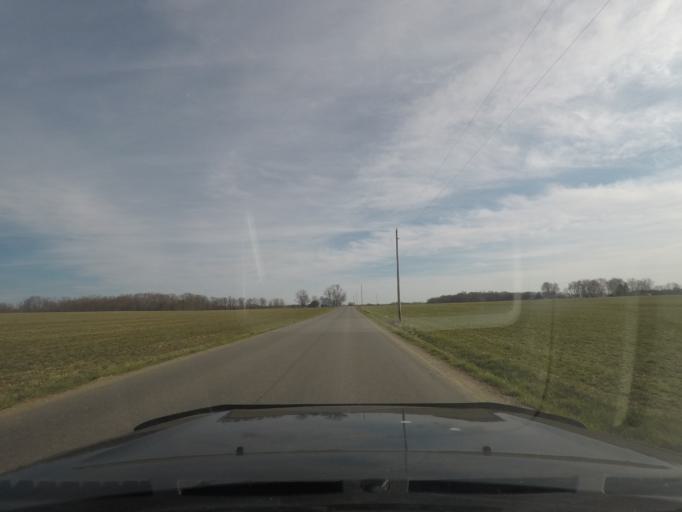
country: US
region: Indiana
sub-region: Elkhart County
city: Dunlap
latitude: 41.5650
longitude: -85.9249
